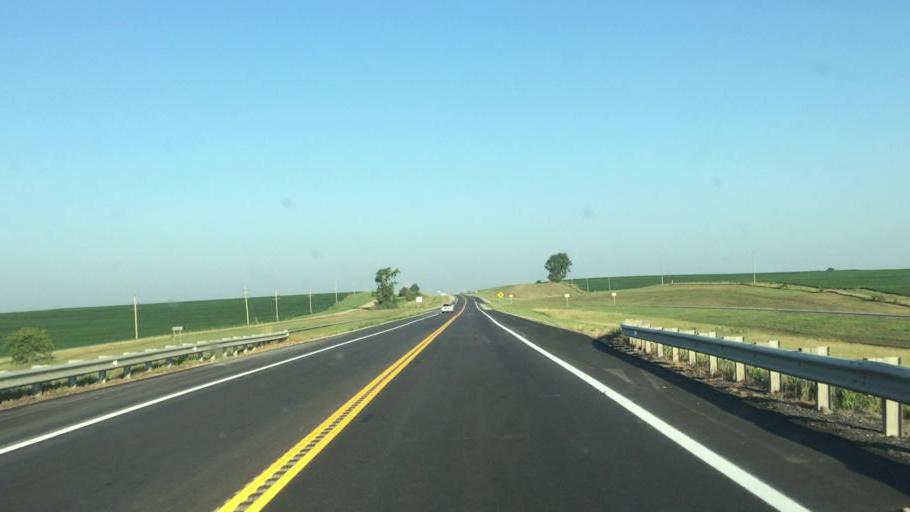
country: US
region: Kansas
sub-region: Brown County
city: Hiawatha
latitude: 39.8416
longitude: -95.4159
